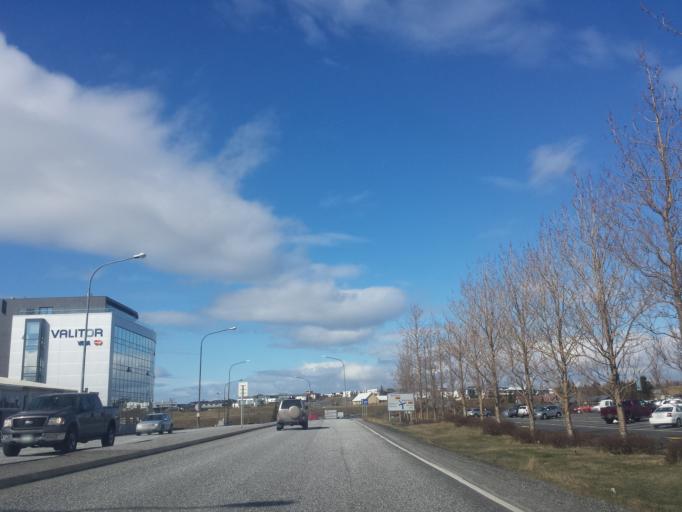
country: IS
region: Capital Region
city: Hafnarfjoerdur
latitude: 64.0817
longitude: -21.9421
